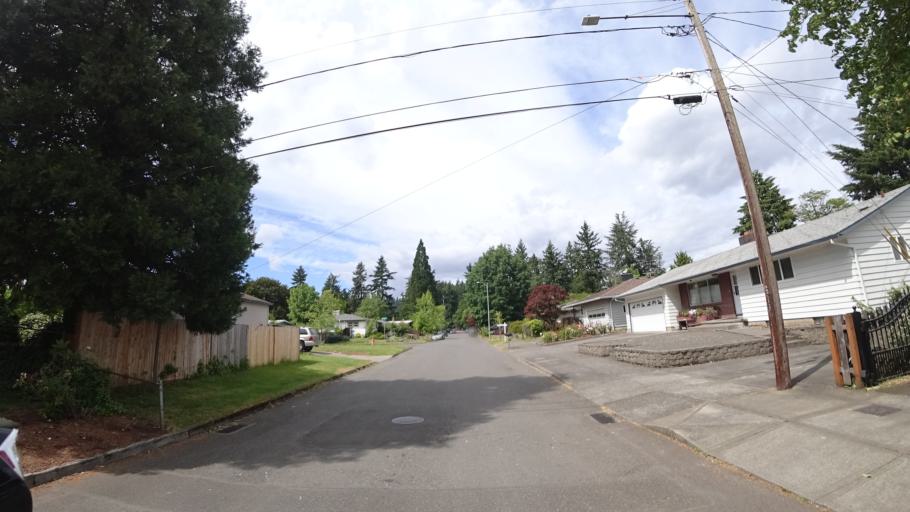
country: US
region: Oregon
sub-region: Multnomah County
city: Lents
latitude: 45.4877
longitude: -122.5514
